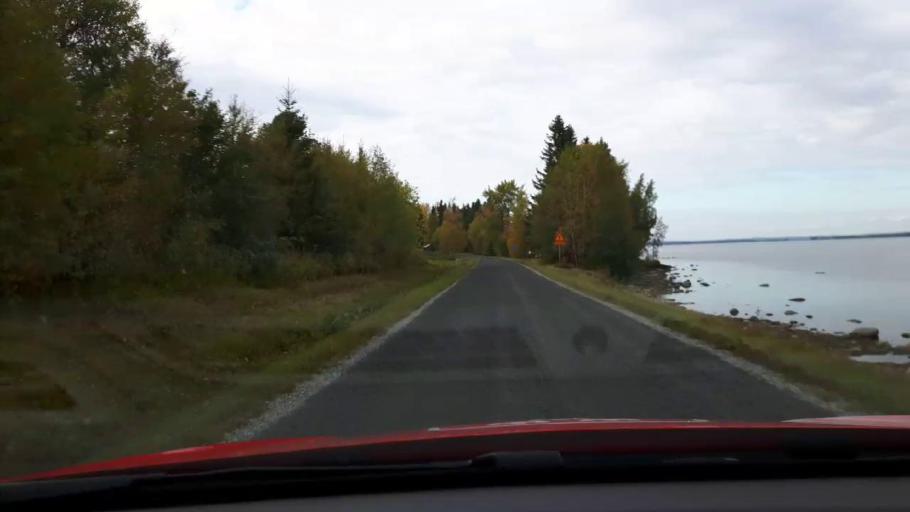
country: SE
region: Jaemtland
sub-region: Krokoms Kommun
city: Krokom
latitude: 63.1629
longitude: 14.1445
